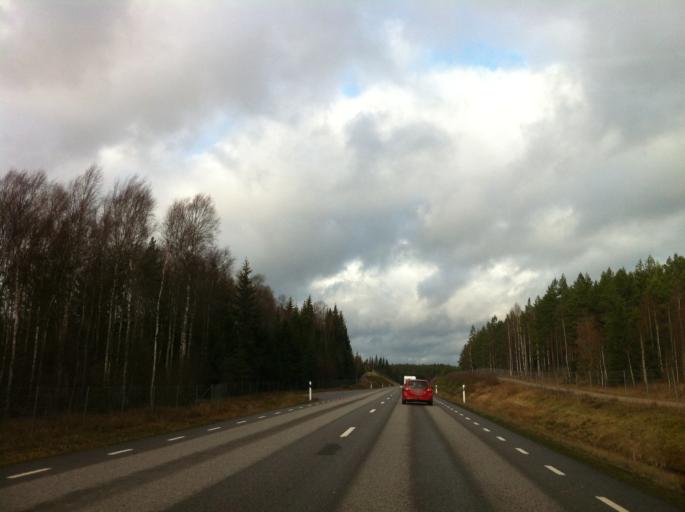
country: SE
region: Kalmar
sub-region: Vimmerby Kommun
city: Vimmerby
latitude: 57.5988
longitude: 15.8470
